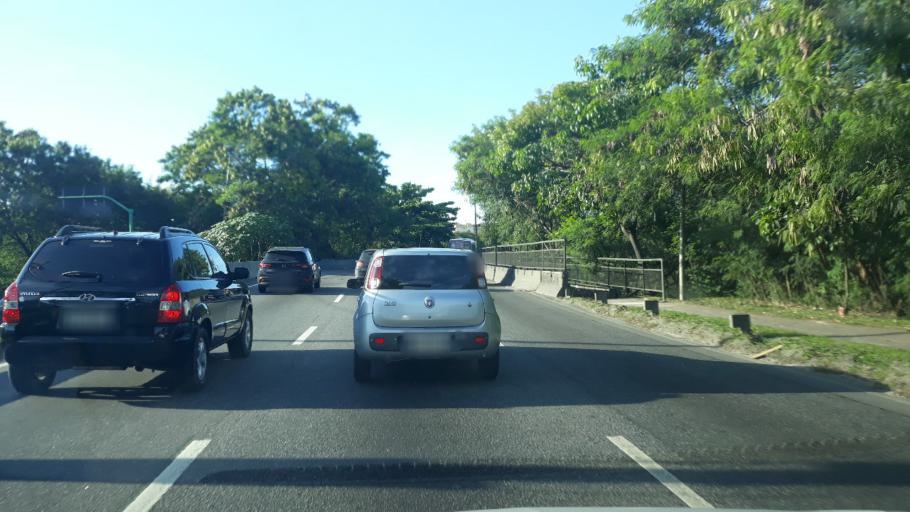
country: BR
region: Rio de Janeiro
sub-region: Rio De Janeiro
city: Rio de Janeiro
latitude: -22.9660
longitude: -43.3573
